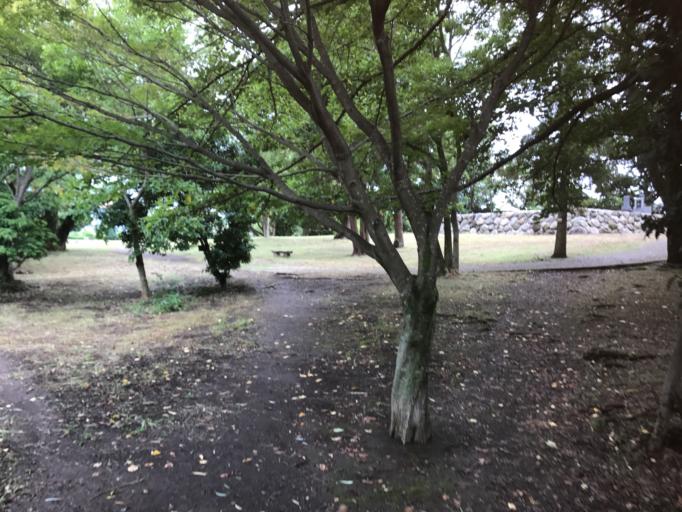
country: JP
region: Shizuoka
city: Numazu
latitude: 35.1296
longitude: 138.8836
